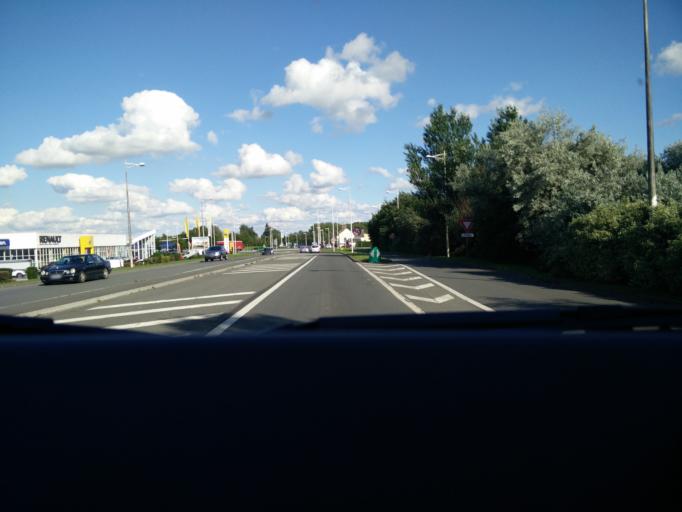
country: FR
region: Nord-Pas-de-Calais
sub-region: Departement du Nord
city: Feignies
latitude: 50.2804
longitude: 3.9061
